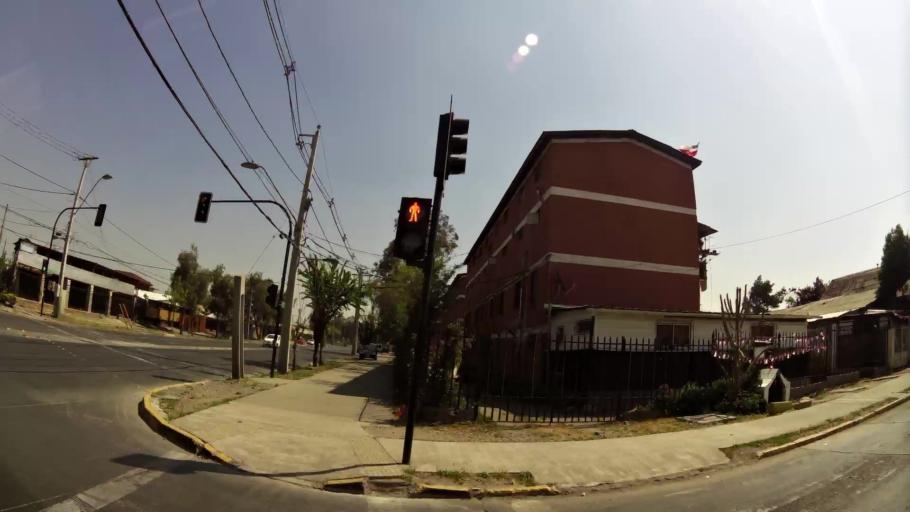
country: CL
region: Santiago Metropolitan
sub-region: Provincia de Santiago
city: La Pintana
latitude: -33.5539
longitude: -70.6108
